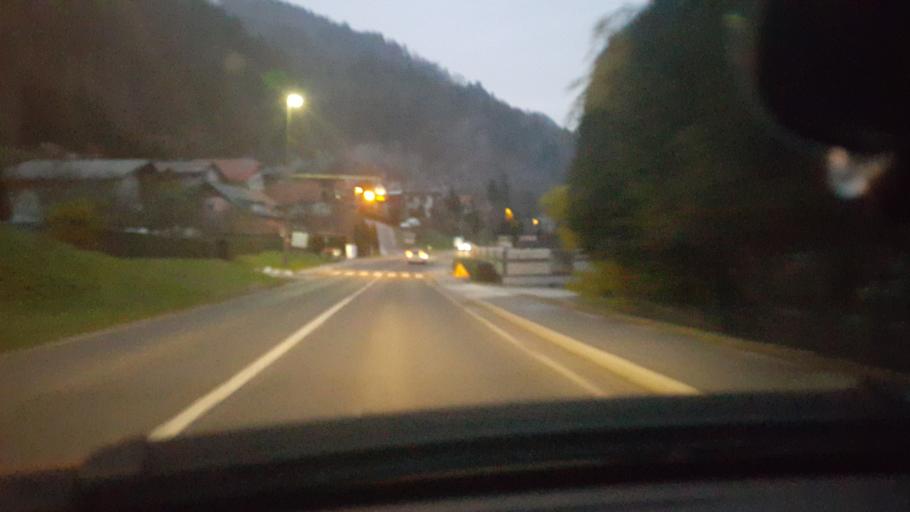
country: SI
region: Dravograd
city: Dravograd
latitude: 46.5937
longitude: 15.0317
